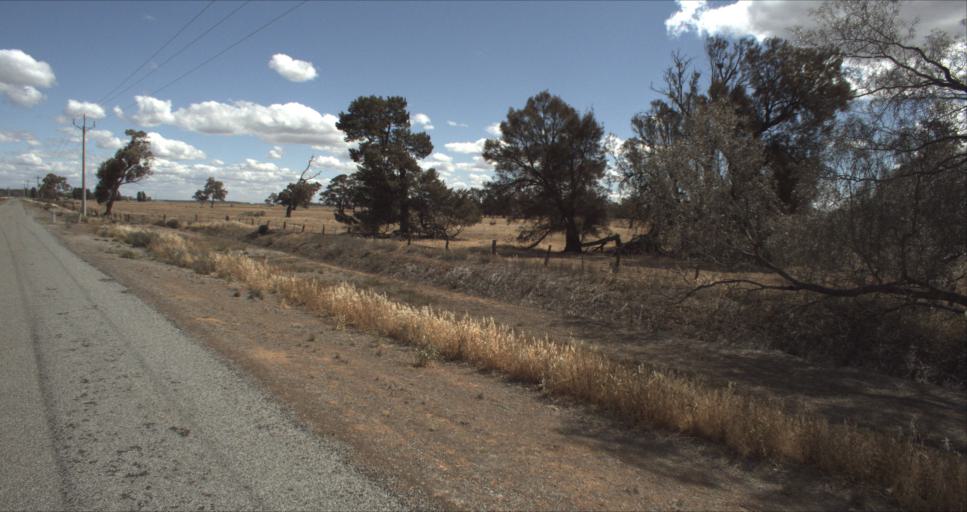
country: AU
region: New South Wales
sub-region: Leeton
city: Leeton
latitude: -34.5195
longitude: 146.2248
